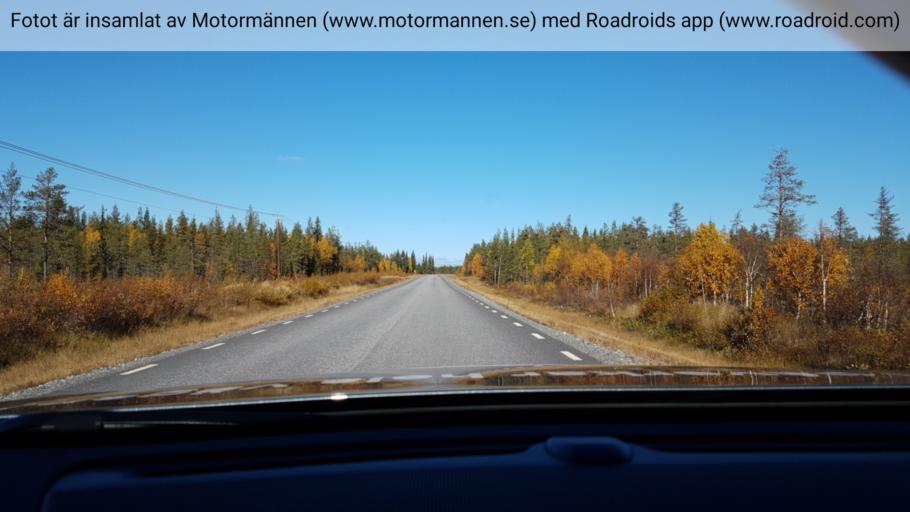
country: SE
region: Norrbotten
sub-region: Gallivare Kommun
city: Gaellivare
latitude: 66.8007
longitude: 21.0390
